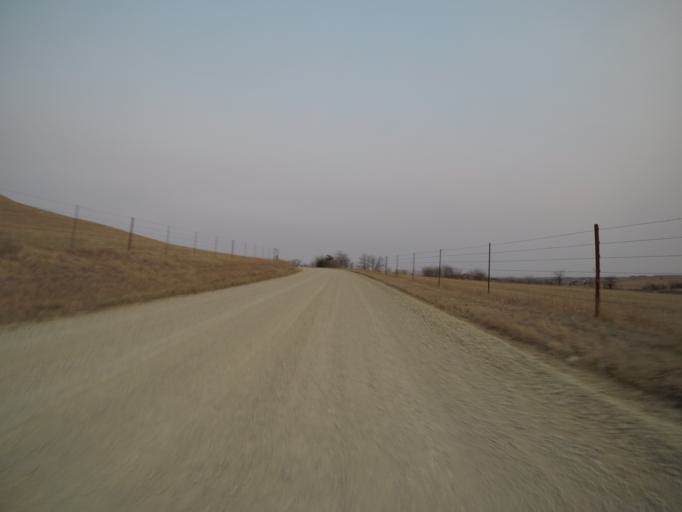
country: US
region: Kansas
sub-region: Riley County
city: Manhattan
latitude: 39.2267
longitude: -96.6364
